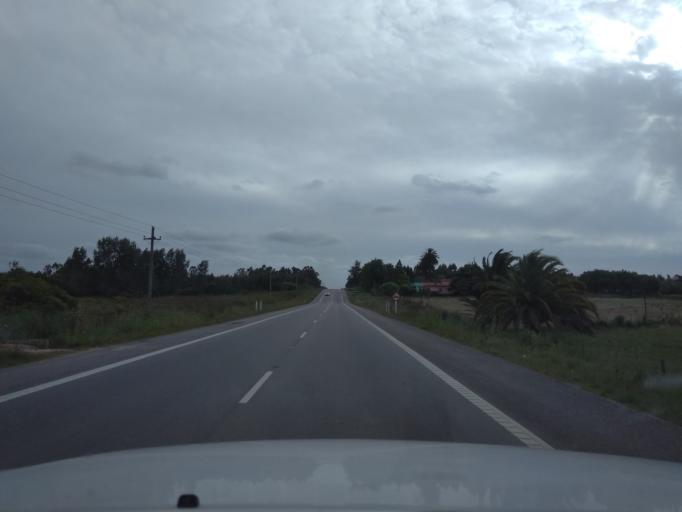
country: UY
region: Canelones
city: Joaquin Suarez
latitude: -34.6888
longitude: -56.0261
